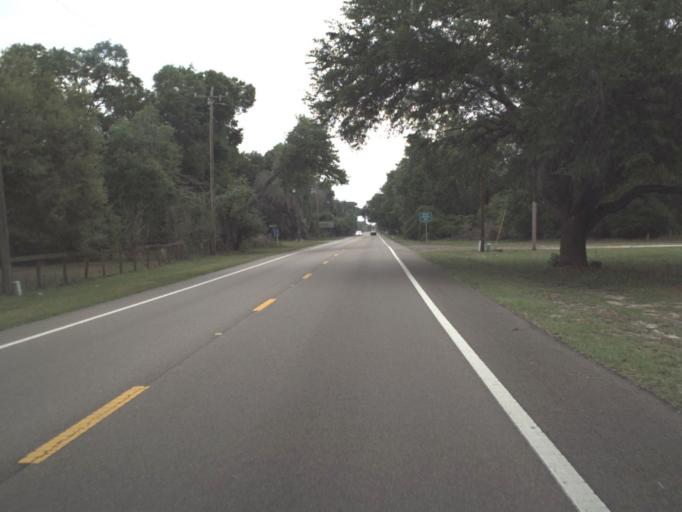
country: US
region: Florida
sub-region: Lake County
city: Umatilla
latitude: 28.9807
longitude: -81.6448
